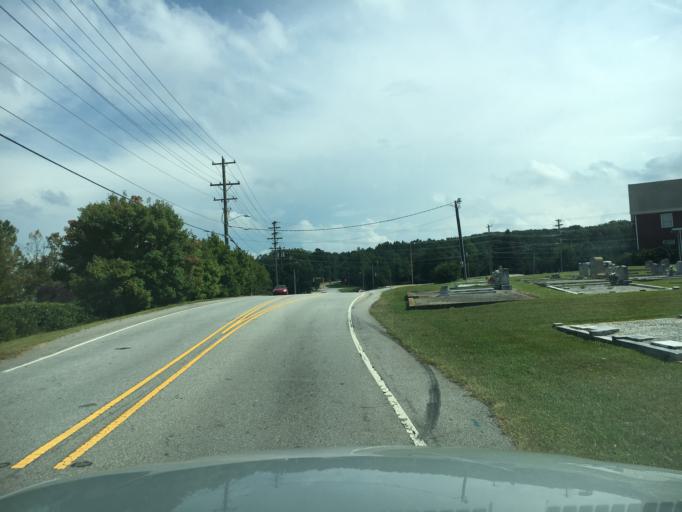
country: US
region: South Carolina
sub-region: Greenville County
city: Wade Hampton
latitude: 34.8461
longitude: -82.3110
